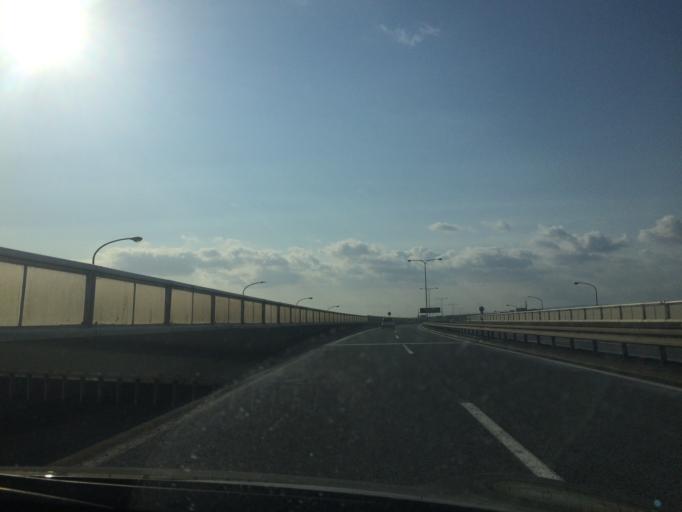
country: JP
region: Hokkaido
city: Sapporo
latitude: 43.0837
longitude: 141.4185
